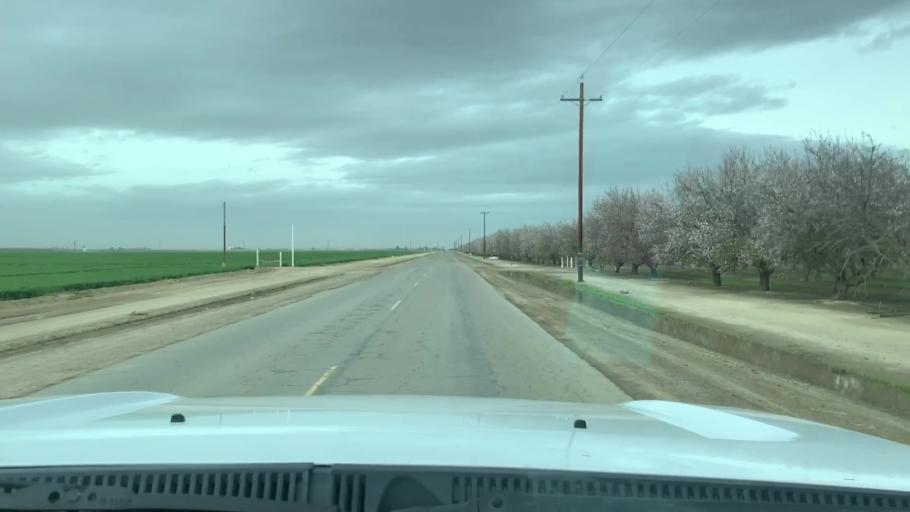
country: US
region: California
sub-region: Kern County
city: Wasco
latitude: 35.5646
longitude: -119.4028
